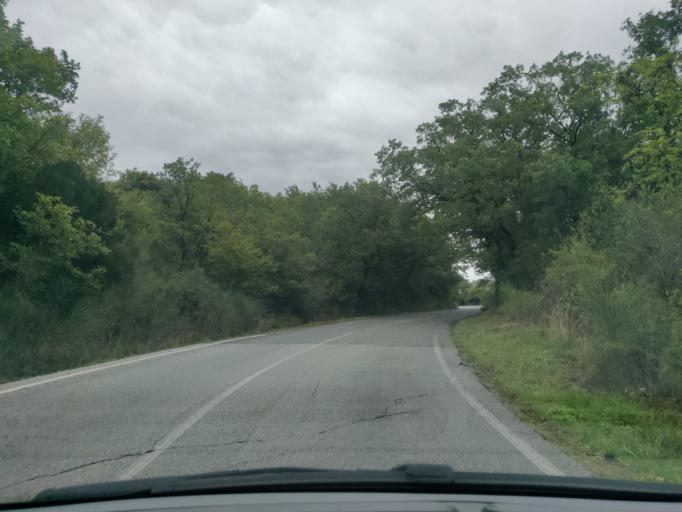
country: IT
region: Latium
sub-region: Citta metropolitana di Roma Capitale
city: Allumiere
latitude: 42.1313
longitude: 11.8676
